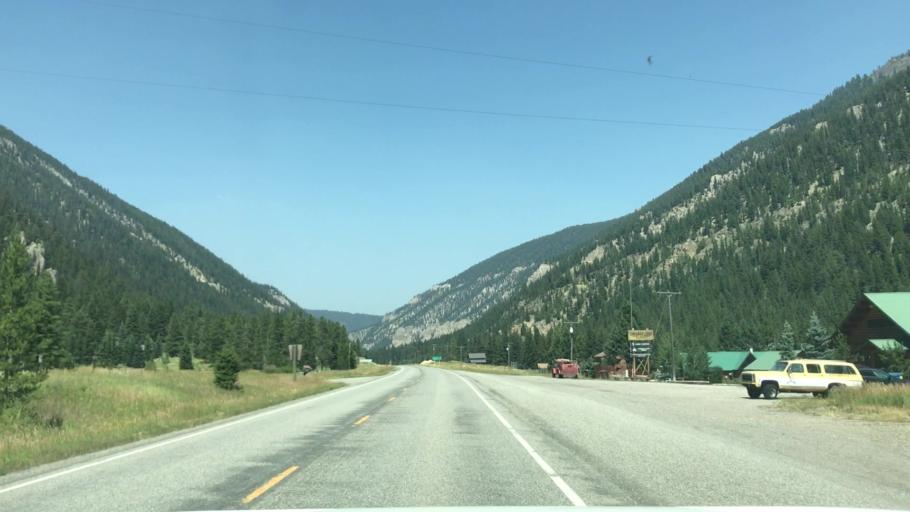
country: US
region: Montana
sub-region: Gallatin County
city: Big Sky
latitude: 45.1156
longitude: -111.2254
